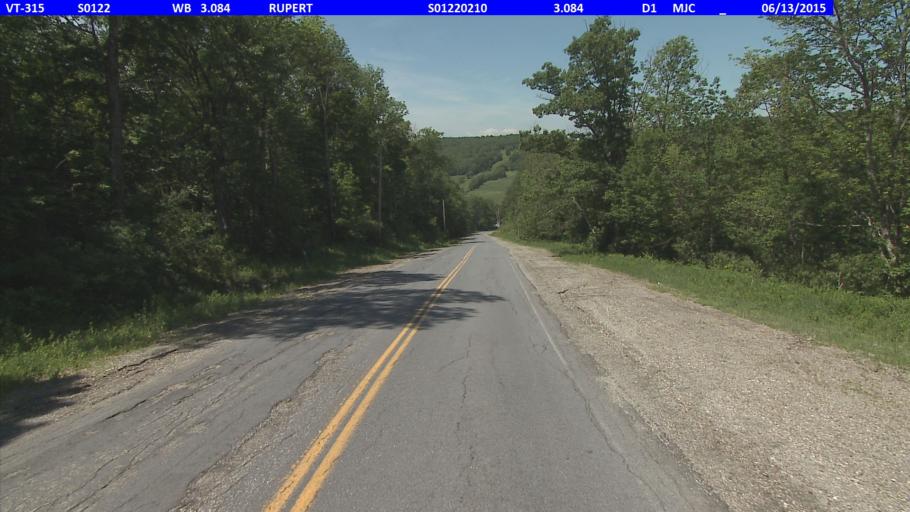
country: US
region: New York
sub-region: Washington County
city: Granville
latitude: 43.2801
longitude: -73.1724
